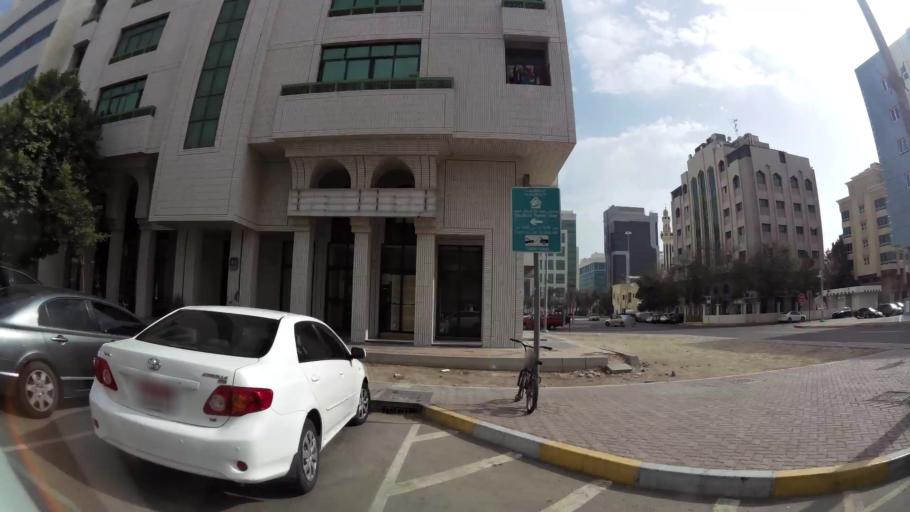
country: AE
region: Abu Dhabi
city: Abu Dhabi
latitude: 24.4621
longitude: 54.3844
